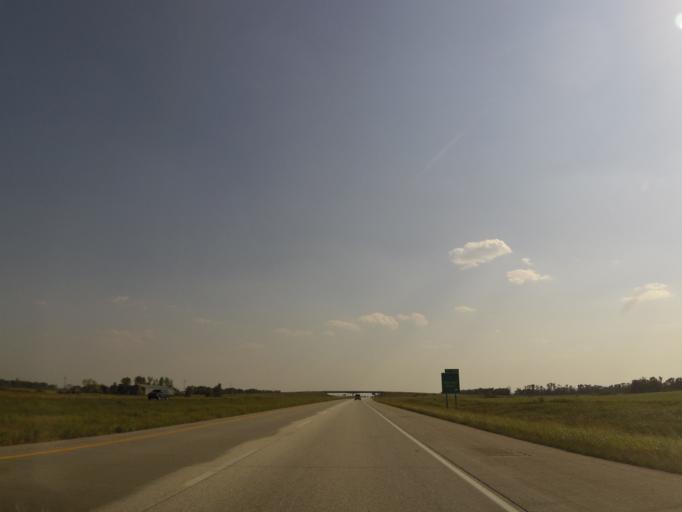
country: US
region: North Dakota
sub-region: Walsh County
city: Grafton
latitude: 48.3011
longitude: -97.1894
